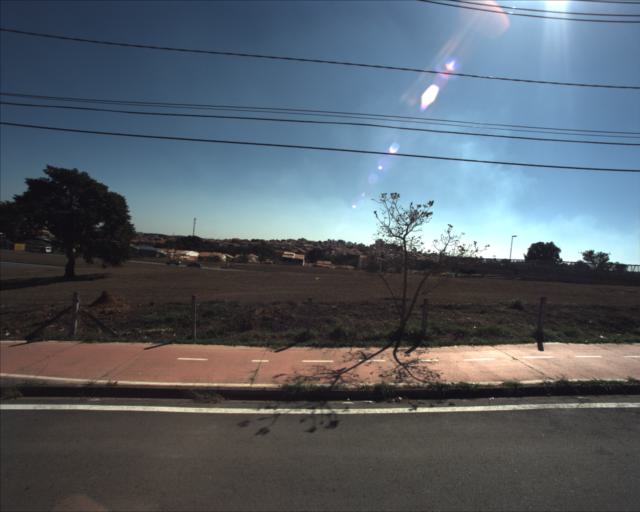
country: BR
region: Sao Paulo
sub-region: Sorocaba
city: Sorocaba
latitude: -23.4738
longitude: -47.4306
